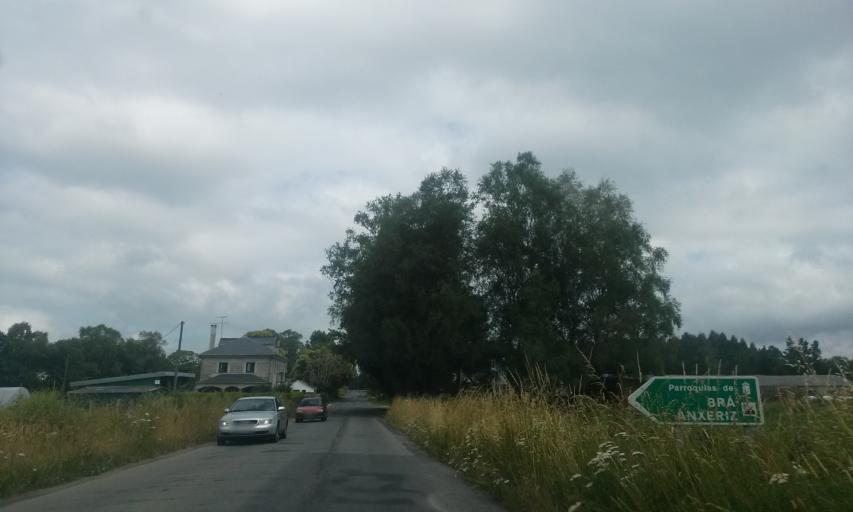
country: ES
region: Galicia
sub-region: Provincia de Lugo
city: Friol
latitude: 43.0912
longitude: -7.8094
